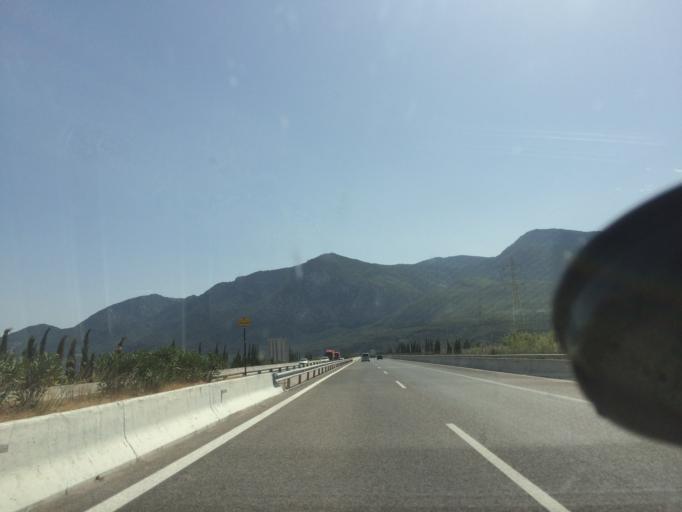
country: GR
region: Central Greece
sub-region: Nomos Fthiotidos
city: Anthili
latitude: 38.8226
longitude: 22.4882
